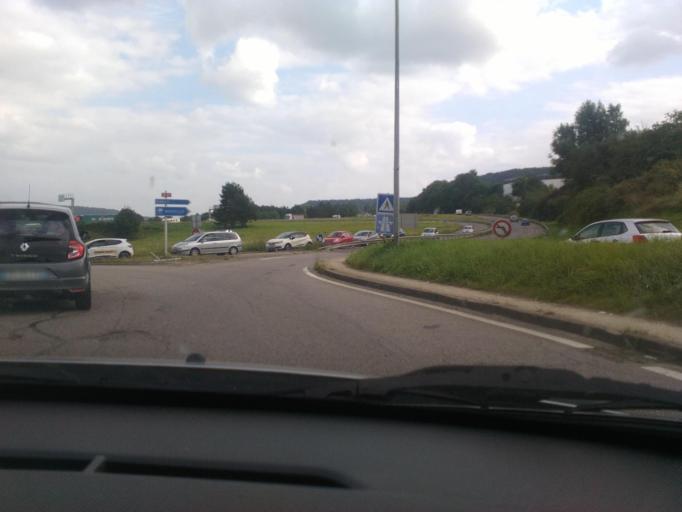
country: FR
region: Lorraine
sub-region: Departement de Meurthe-et-Moselle
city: Champigneulles
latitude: 48.7454
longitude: 6.1510
